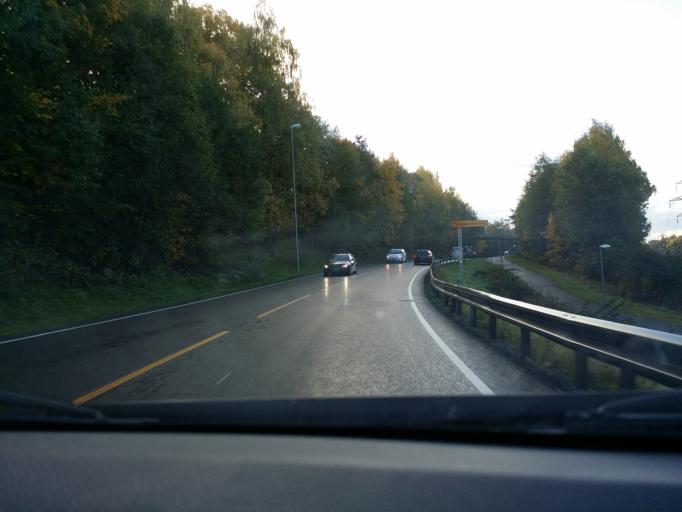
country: NO
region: Akershus
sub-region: Baerum
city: Sandvika
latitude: 59.9269
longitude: 10.4971
